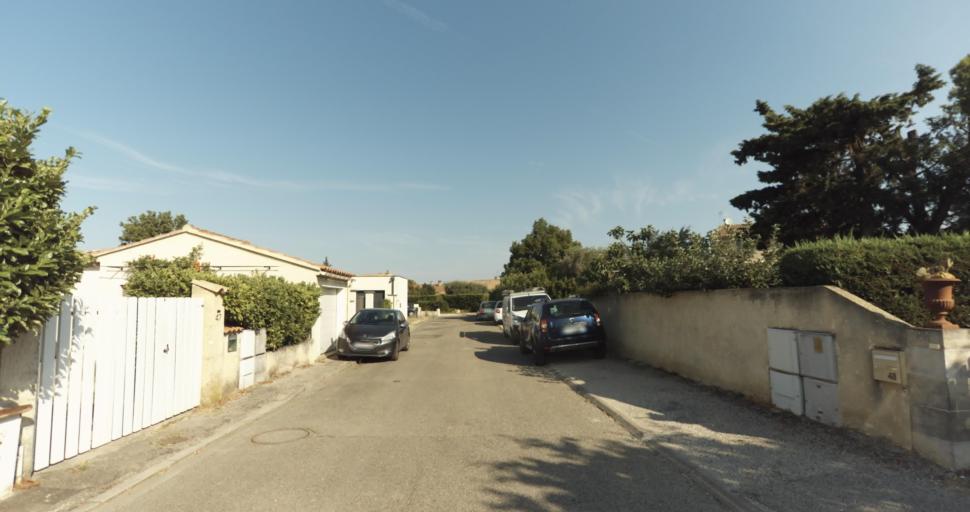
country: FR
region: Provence-Alpes-Cote d'Azur
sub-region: Departement du Vaucluse
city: Monteux
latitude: 44.0343
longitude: 5.0147
